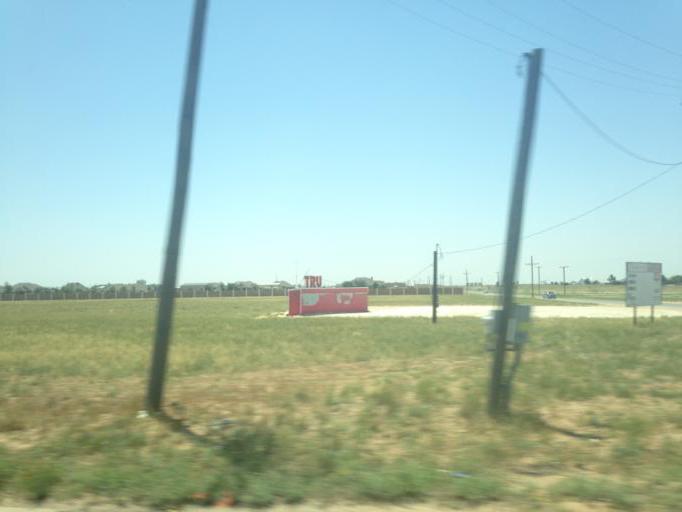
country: US
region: Texas
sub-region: Midland County
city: Midland
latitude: 32.0570
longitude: -102.0299
